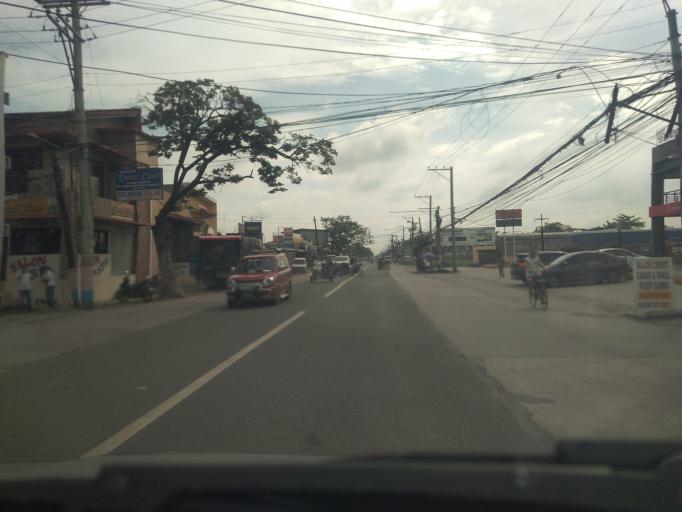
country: PH
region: Central Luzon
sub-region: Province of Pampanga
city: Pau
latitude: 15.0079
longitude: 120.7120
